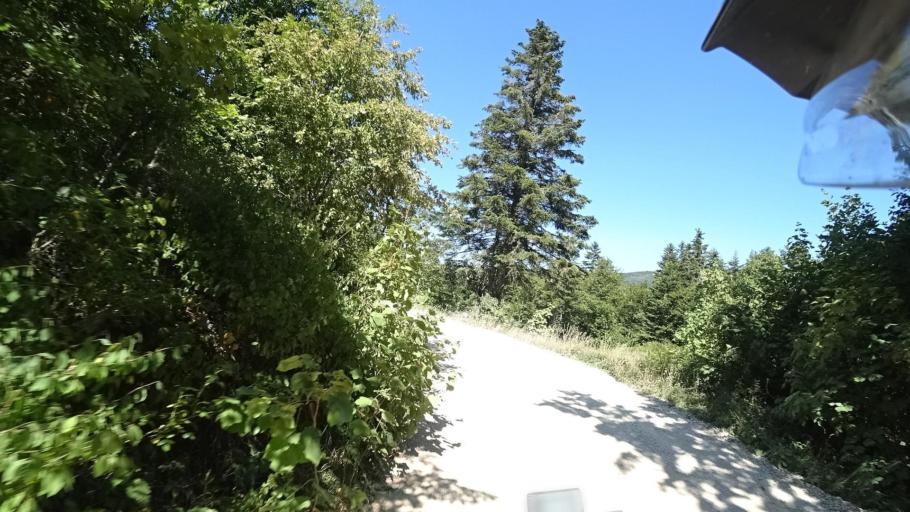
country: HR
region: Licko-Senjska
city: Otocac
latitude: 44.7901
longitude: 15.3992
